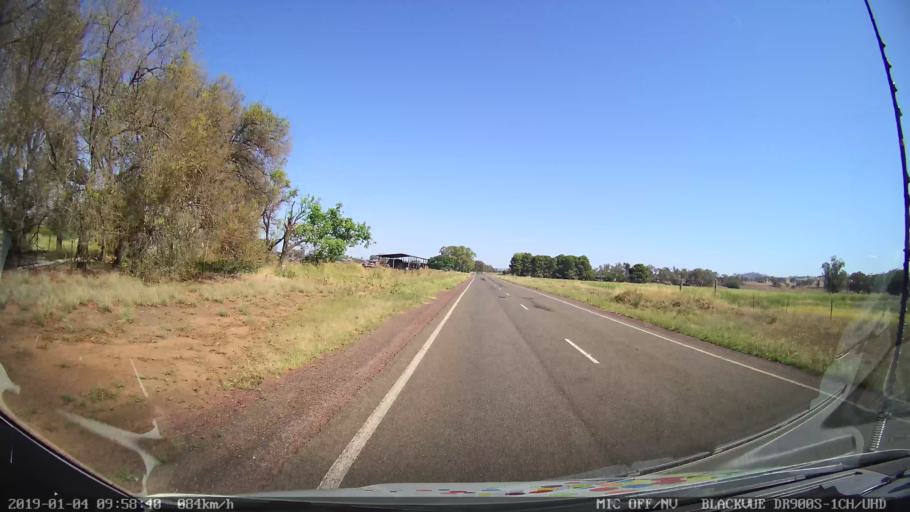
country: AU
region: New South Wales
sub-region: Cabonne
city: Canowindra
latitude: -33.5161
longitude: 148.3926
